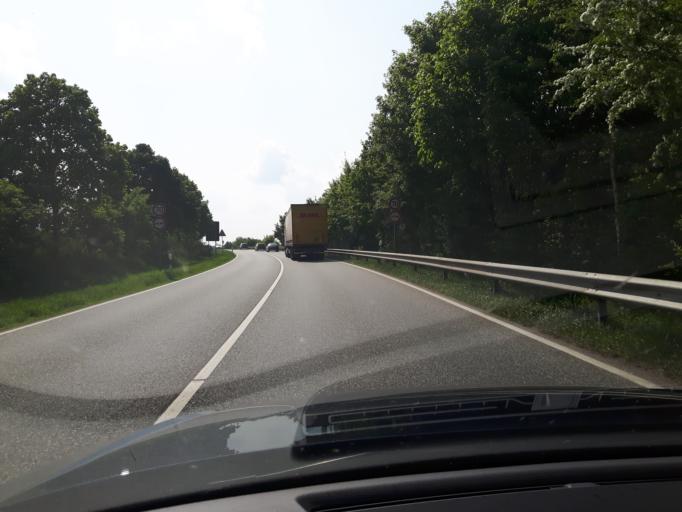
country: DE
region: Mecklenburg-Vorpommern
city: Selmsdorf
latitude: 53.8836
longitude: 10.8202
